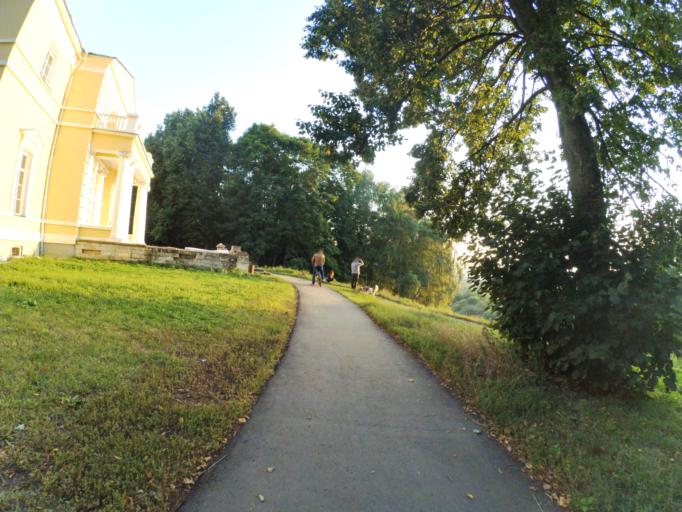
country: RU
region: Moscow
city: Strogino
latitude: 55.8487
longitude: 37.3975
